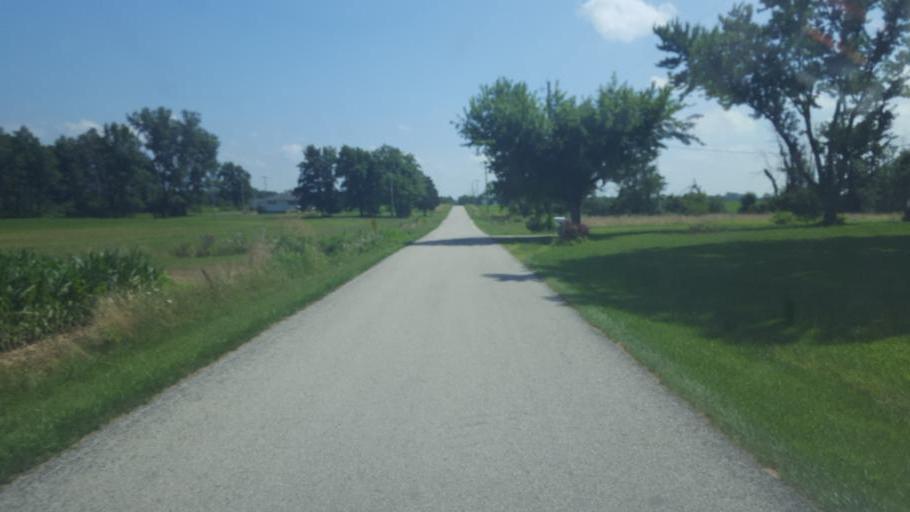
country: US
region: Ohio
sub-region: Huron County
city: Willard
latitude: 41.1312
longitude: -82.8147
